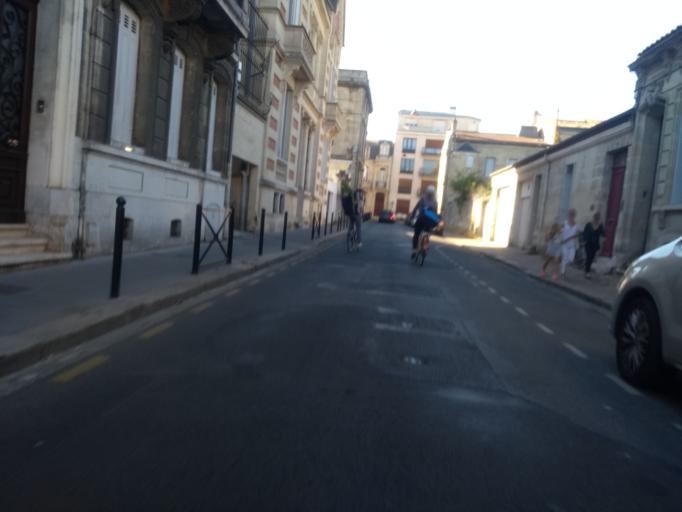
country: FR
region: Aquitaine
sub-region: Departement de la Gironde
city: Bordeaux
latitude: 44.8260
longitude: -0.5799
